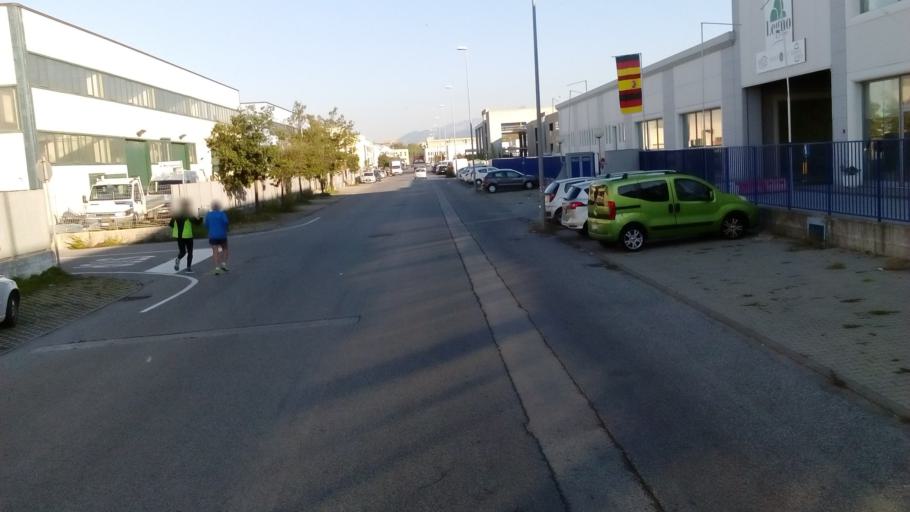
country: IT
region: Tuscany
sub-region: Provincia di Lucca
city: Viareggio
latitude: 43.8573
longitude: 10.2754
